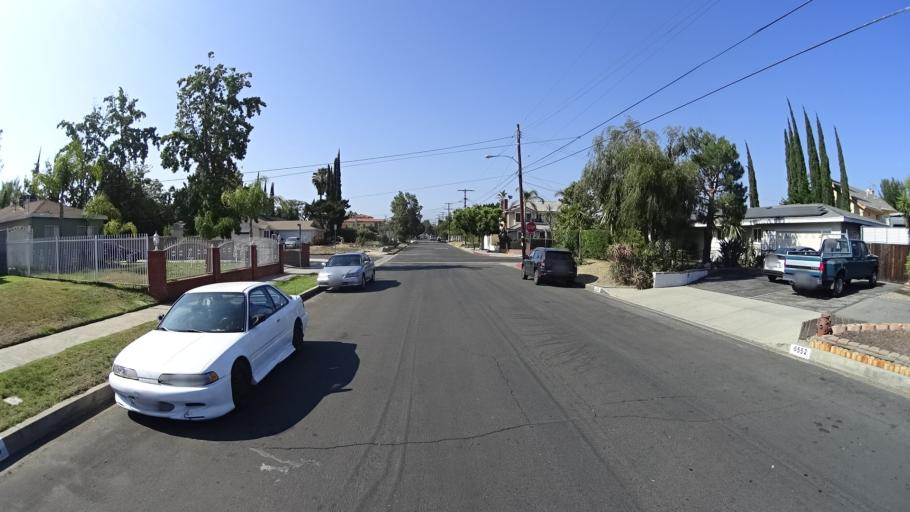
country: US
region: California
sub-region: Los Angeles County
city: Van Nuys
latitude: 34.1899
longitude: -118.4259
